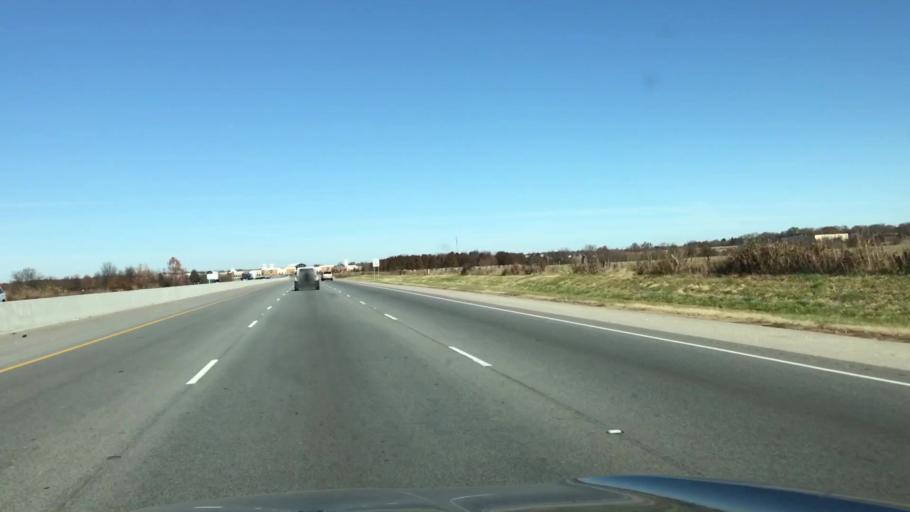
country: US
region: Arkansas
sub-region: Benton County
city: Lowell
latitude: 36.2675
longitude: -94.1507
